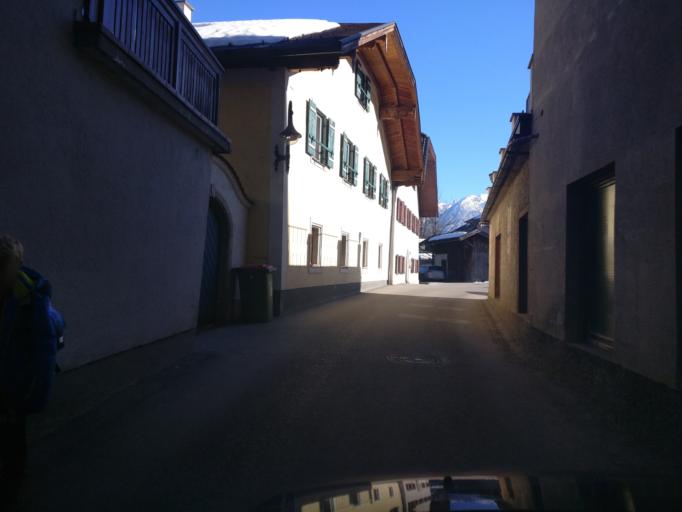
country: AT
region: Salzburg
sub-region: Politischer Bezirk Hallein
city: Kuchl
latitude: 47.6257
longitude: 13.1442
